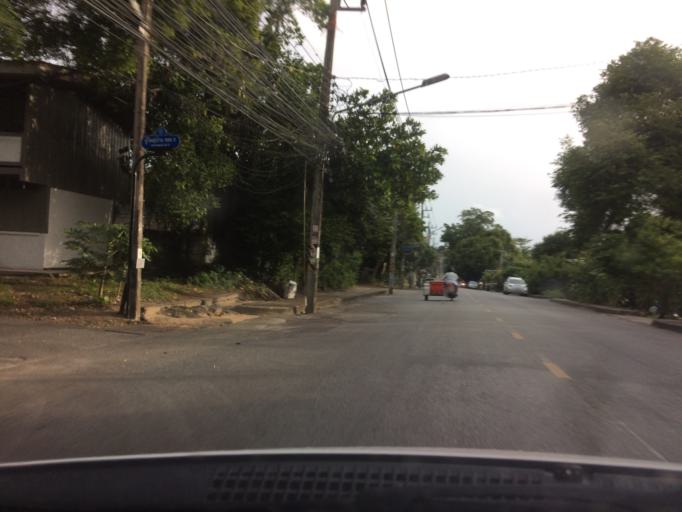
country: TH
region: Phuket
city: Ban Talat Yai
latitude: 7.8892
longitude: 98.4054
